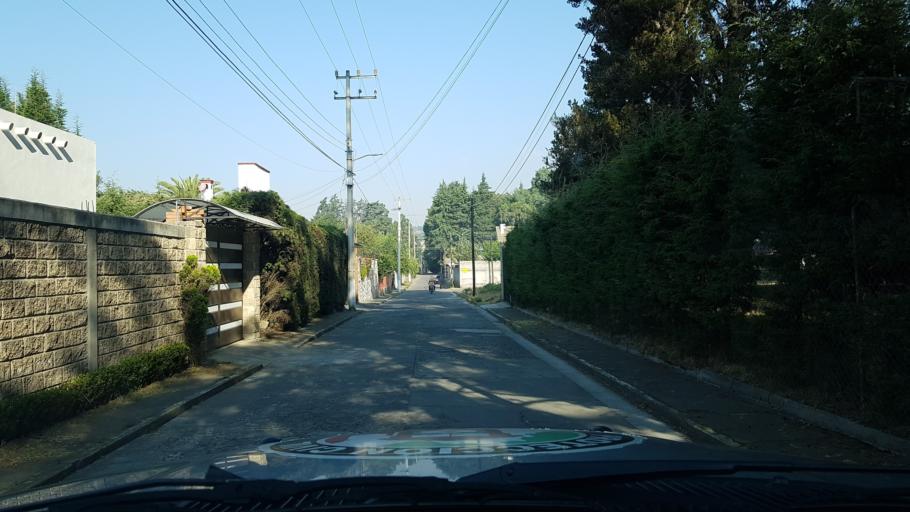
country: MX
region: Mexico
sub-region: Amecameca
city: San Diego Huehuecalco
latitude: 19.0720
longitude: -98.7772
